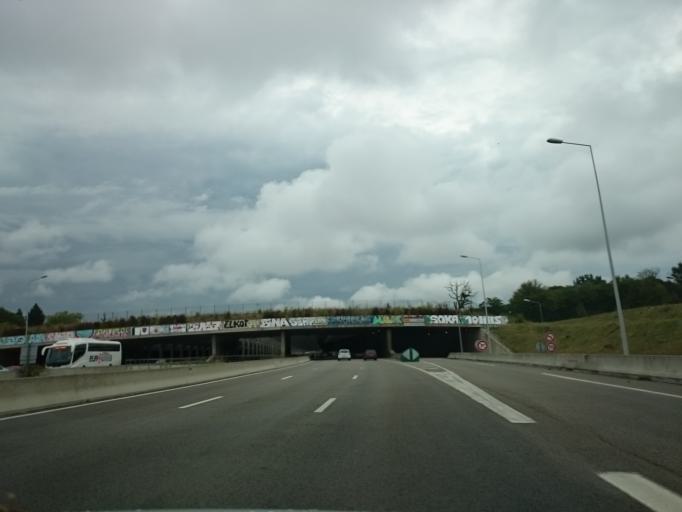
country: FR
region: Ile-de-France
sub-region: Departement des Yvelines
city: Viroflay
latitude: 48.7817
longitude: 2.1630
